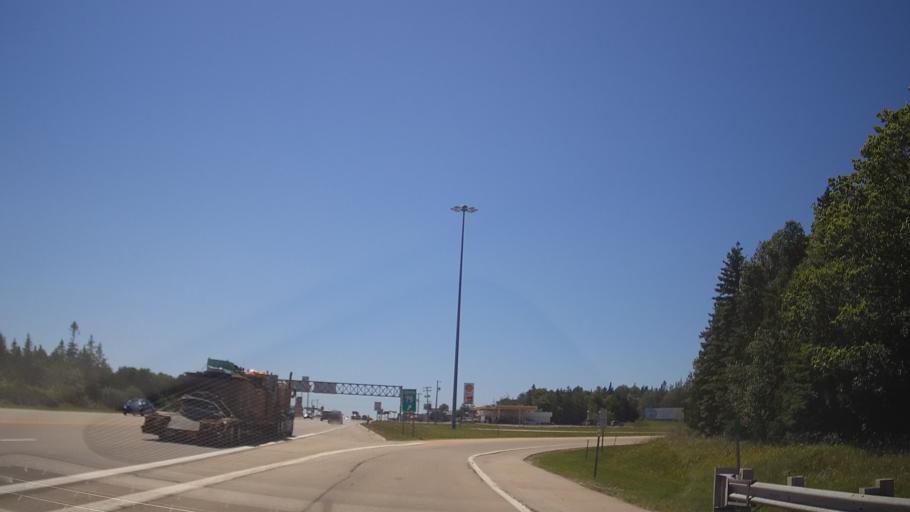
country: US
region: Michigan
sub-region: Mackinac County
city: Saint Ignace
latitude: 45.8574
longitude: -84.7298
